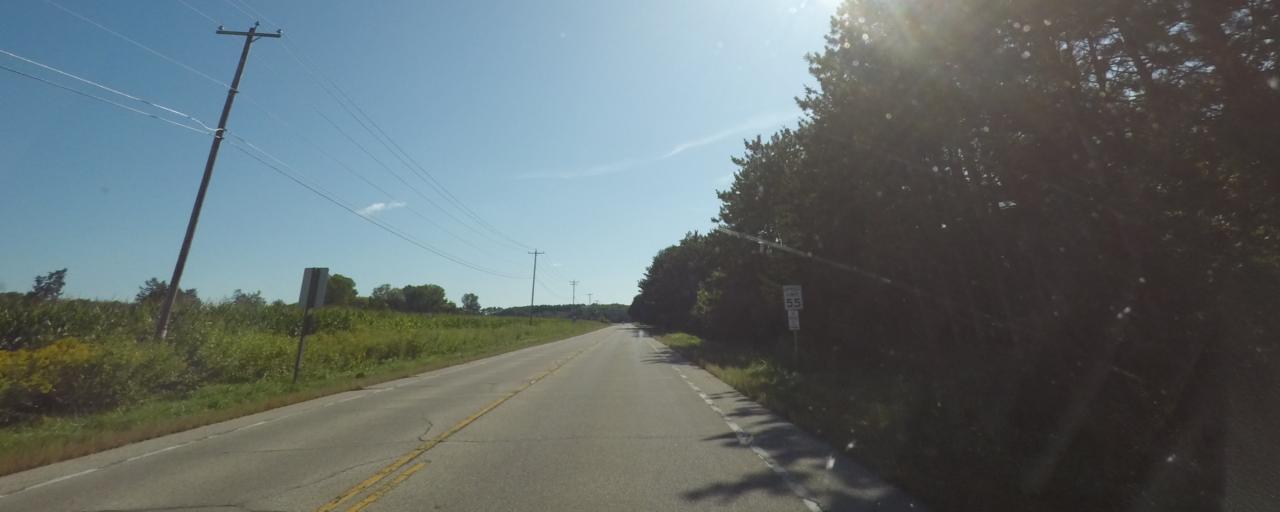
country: US
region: Wisconsin
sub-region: Waukesha County
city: Dousman
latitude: 43.0274
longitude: -88.5272
